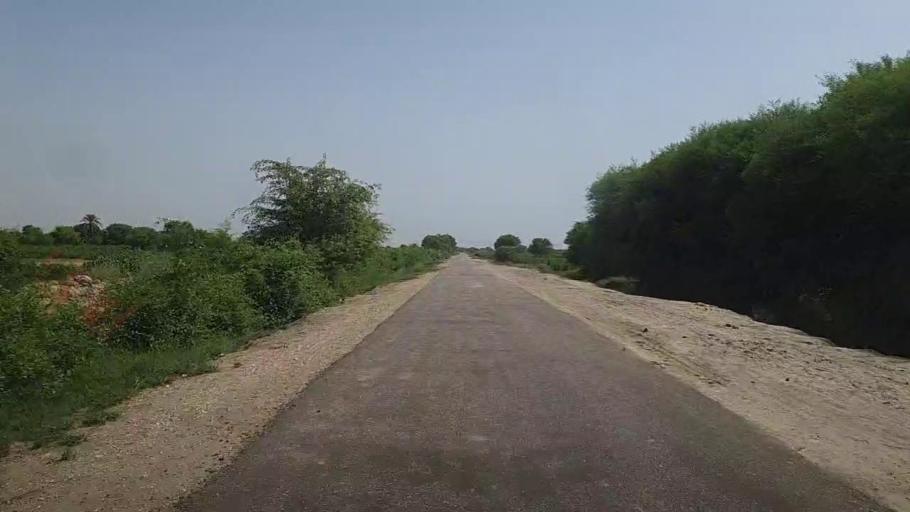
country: PK
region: Sindh
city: Pad Idan
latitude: 26.8381
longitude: 68.3307
